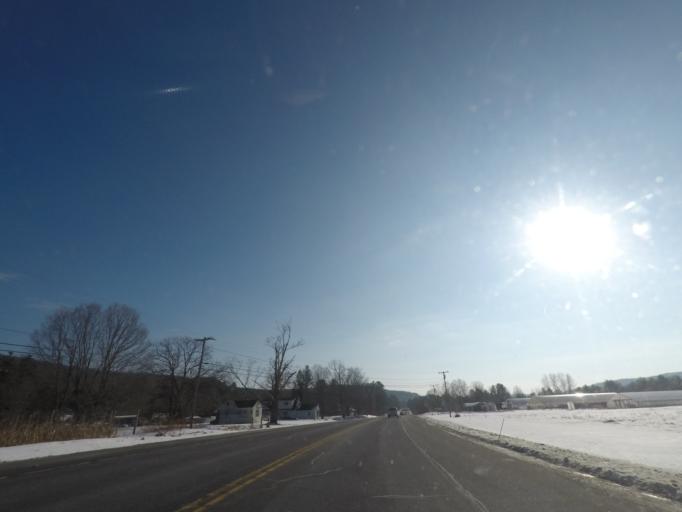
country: US
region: Massachusetts
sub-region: Berkshire County
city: Lanesborough
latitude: 42.5282
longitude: -73.3562
